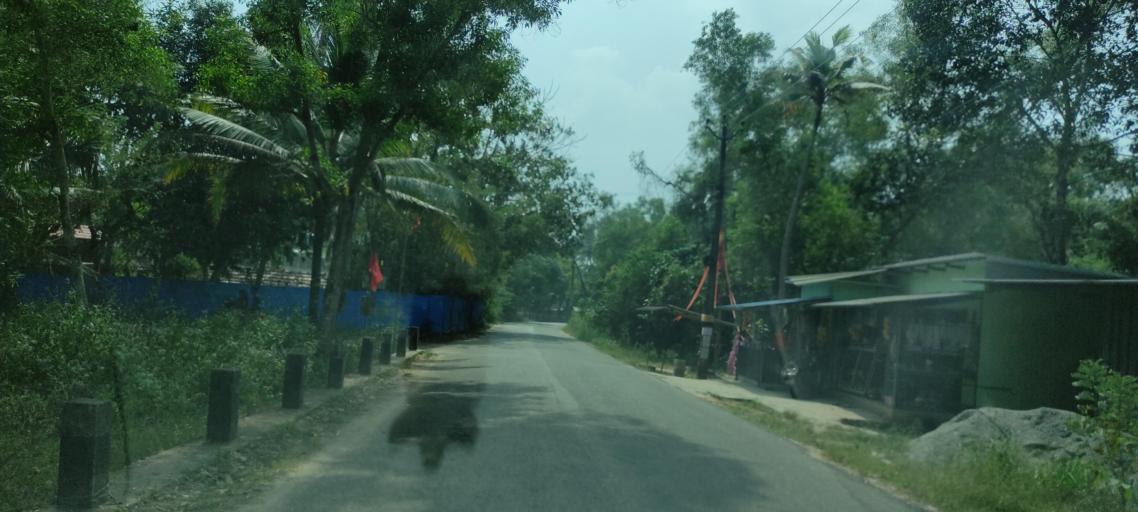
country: IN
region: Kerala
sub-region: Alappuzha
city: Shertallai
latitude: 9.6309
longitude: 76.3518
